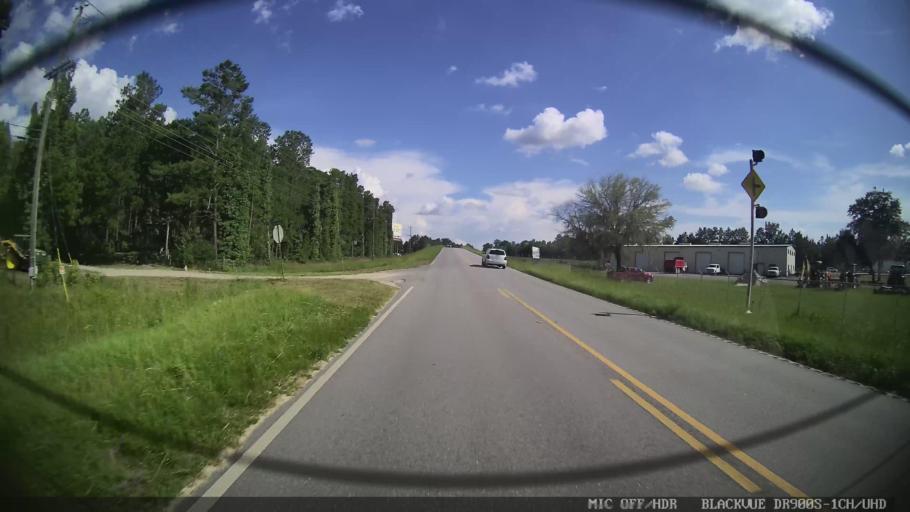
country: US
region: Georgia
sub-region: Lowndes County
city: Valdosta
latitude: 30.6975
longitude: -83.2386
